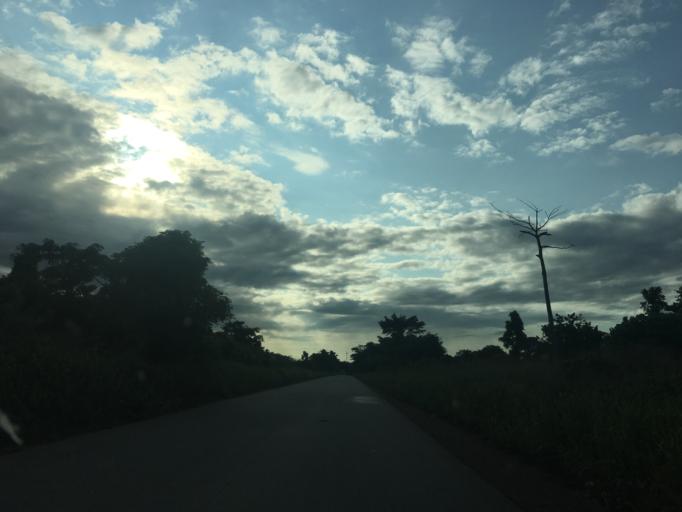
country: GH
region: Western
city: Bibiani
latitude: 6.2970
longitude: -2.2387
